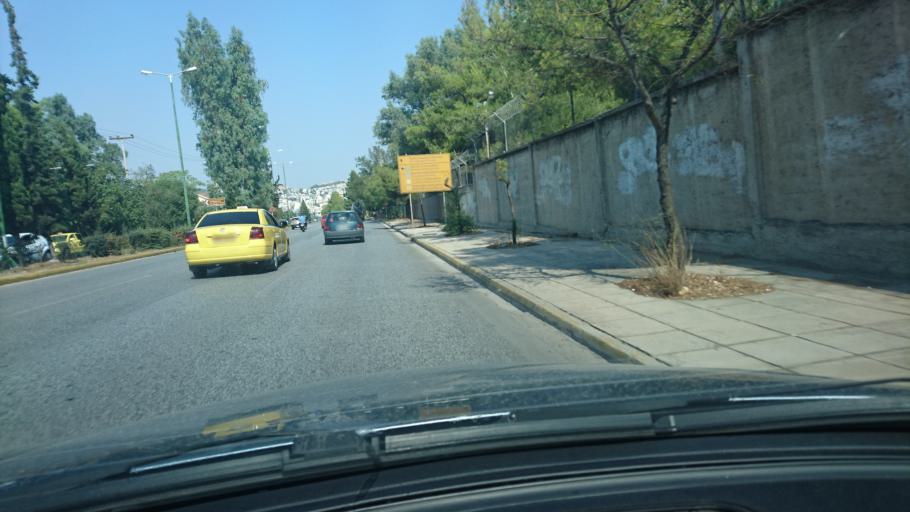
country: GR
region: Attica
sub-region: Nomarchia Athinas
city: Papagou
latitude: 37.9850
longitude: 23.7823
